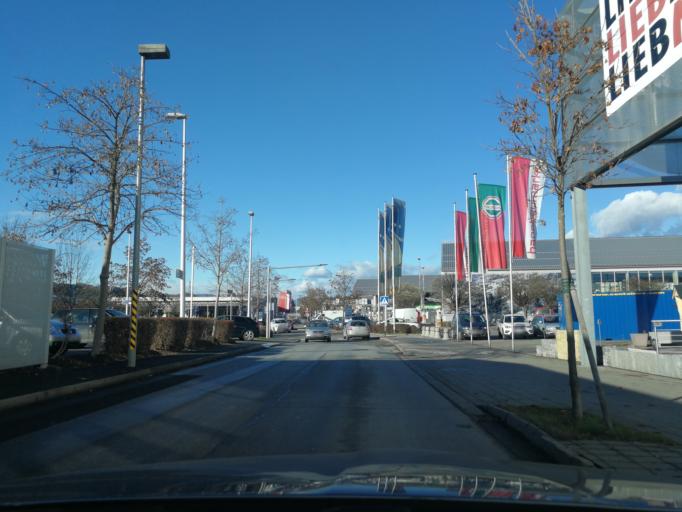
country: AT
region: Styria
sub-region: Politischer Bezirk Weiz
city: Gleisdorf
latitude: 47.1063
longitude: 15.7056
